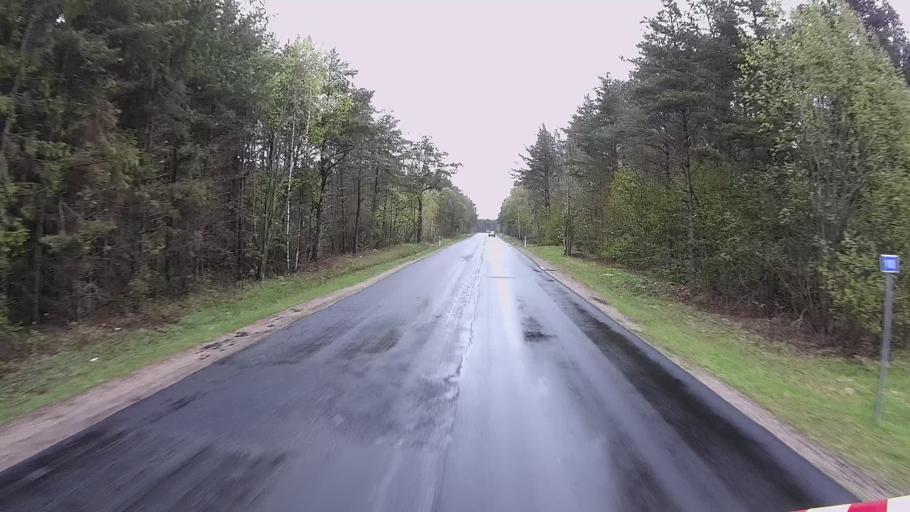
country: EE
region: Saare
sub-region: Kuressaare linn
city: Kuressaare
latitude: 58.3596
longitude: 22.6066
